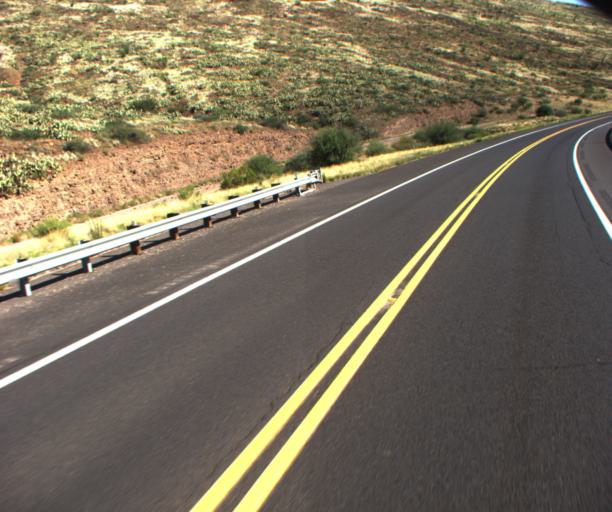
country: US
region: Arizona
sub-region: Greenlee County
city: Clifton
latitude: 32.8953
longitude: -109.2721
